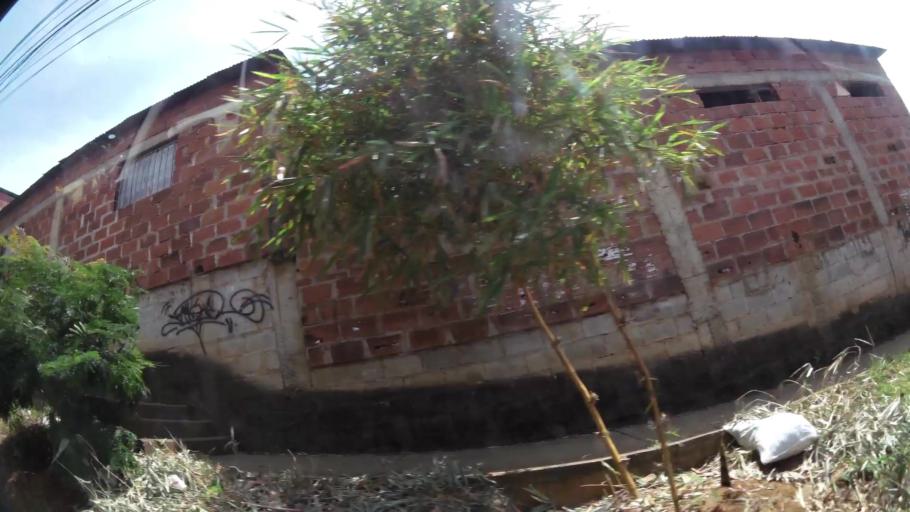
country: CO
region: Antioquia
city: Bello
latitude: 6.3455
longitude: -75.5456
